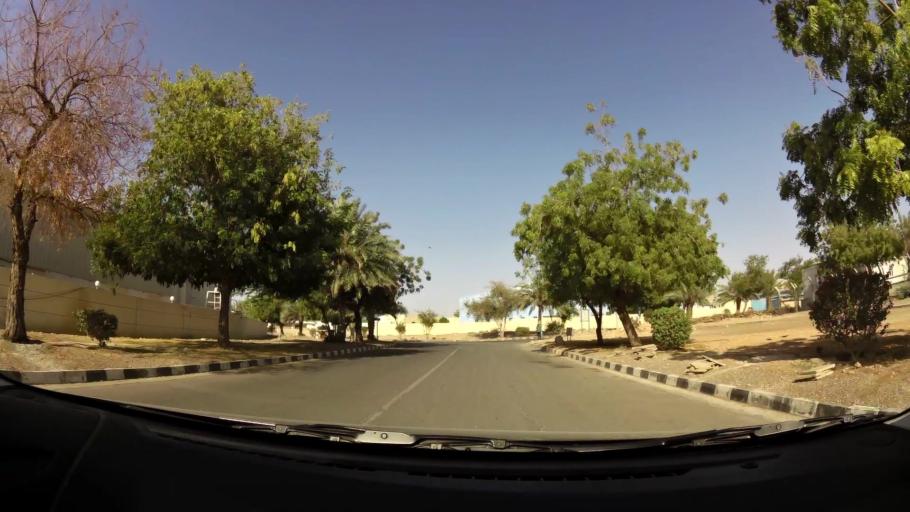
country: OM
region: Muhafazat Masqat
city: As Sib al Jadidah
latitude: 23.5552
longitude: 58.2014
